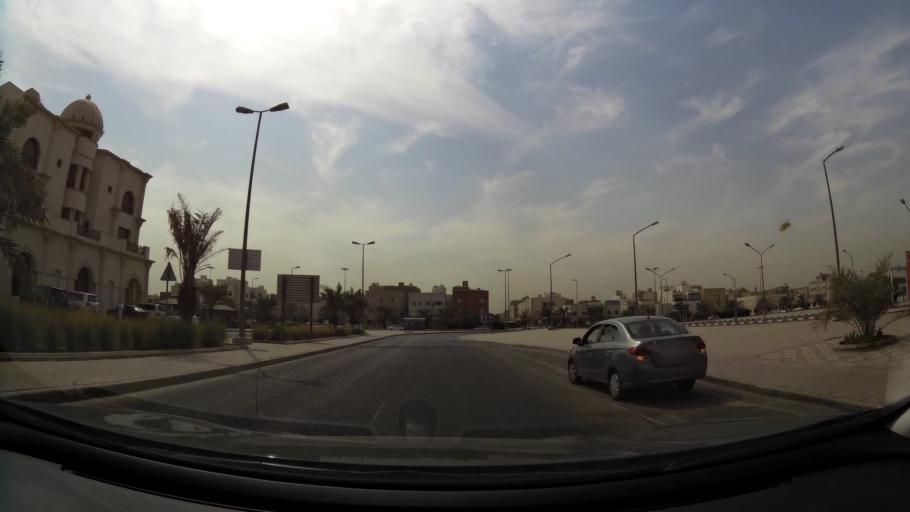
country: KW
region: Al Farwaniyah
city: Janub as Surrah
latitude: 29.2850
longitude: 48.0072
